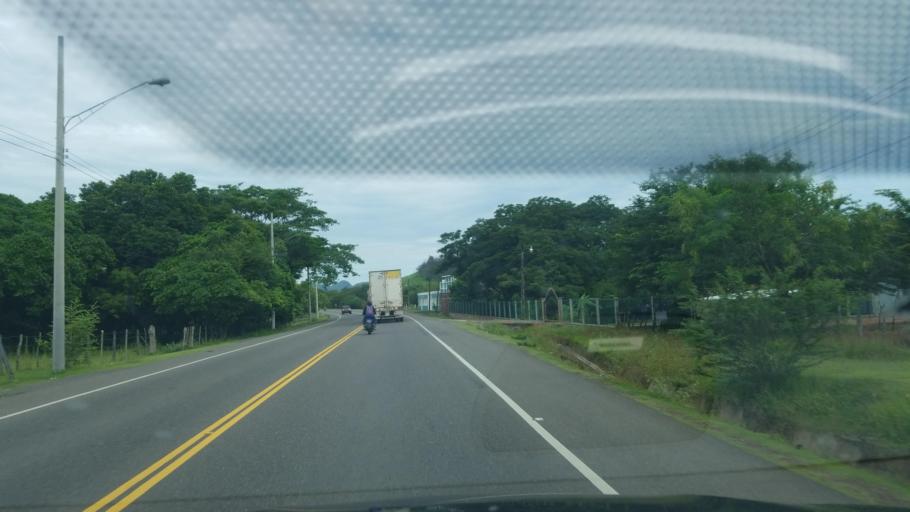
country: HN
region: Valle
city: Goascoran
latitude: 13.5391
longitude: -87.6045
